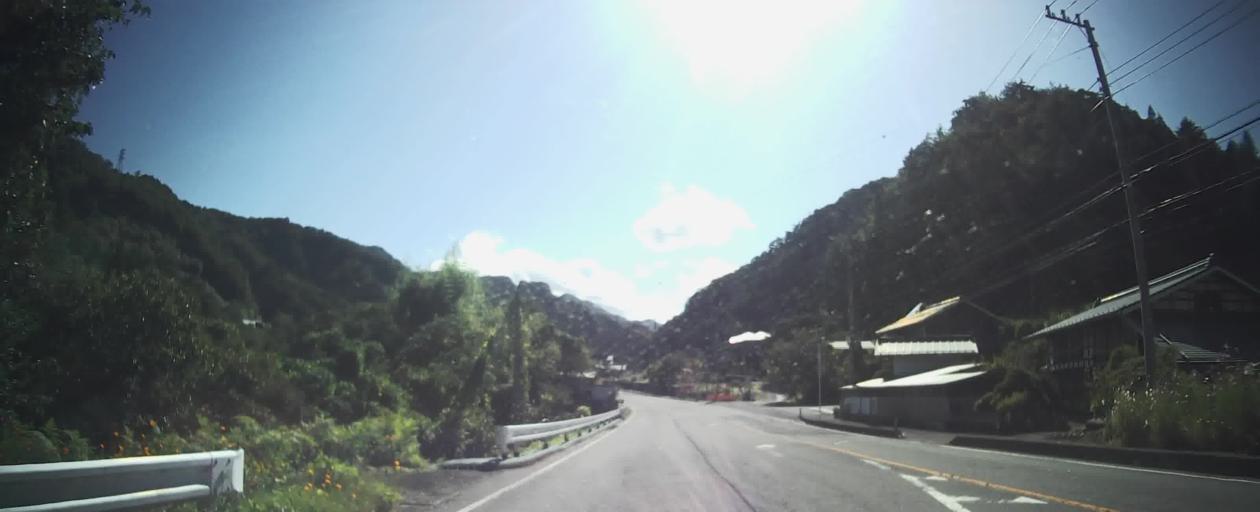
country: JP
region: Gunma
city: Nakanojomachi
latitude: 36.5692
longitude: 138.7309
